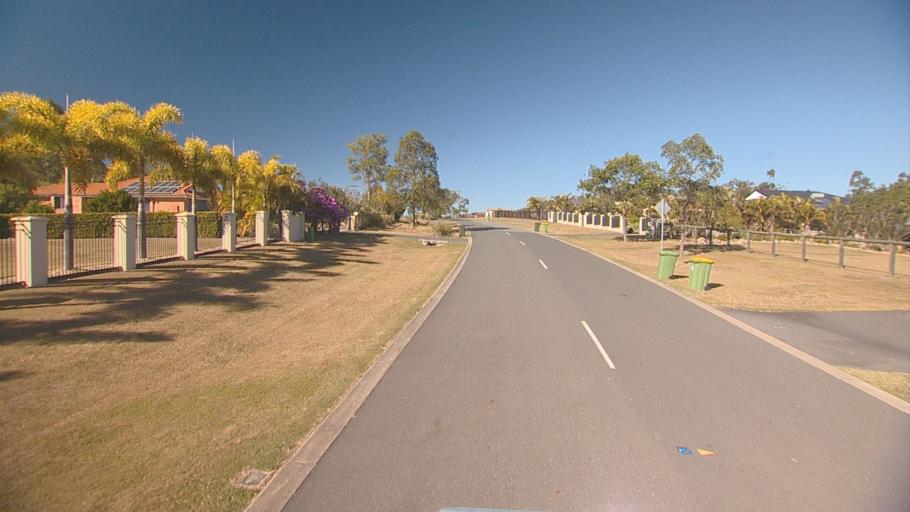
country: AU
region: Queensland
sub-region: Logan
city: North Maclean
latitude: -27.7546
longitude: 152.9568
